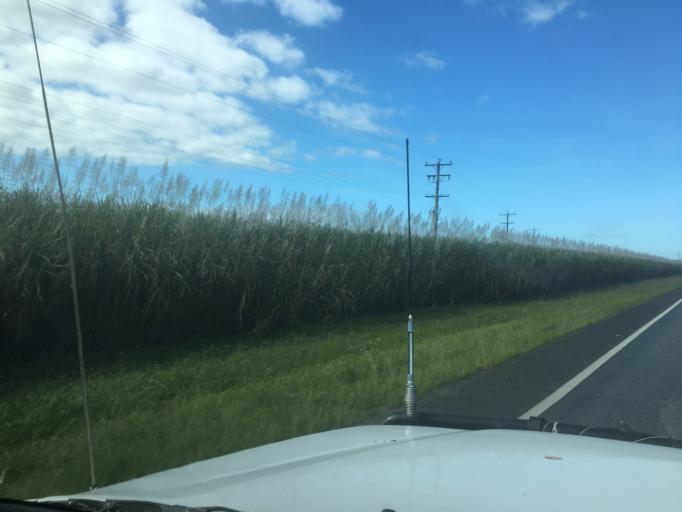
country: AU
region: Queensland
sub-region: Cassowary Coast
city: Innisfail
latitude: -17.3005
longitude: 145.9280
